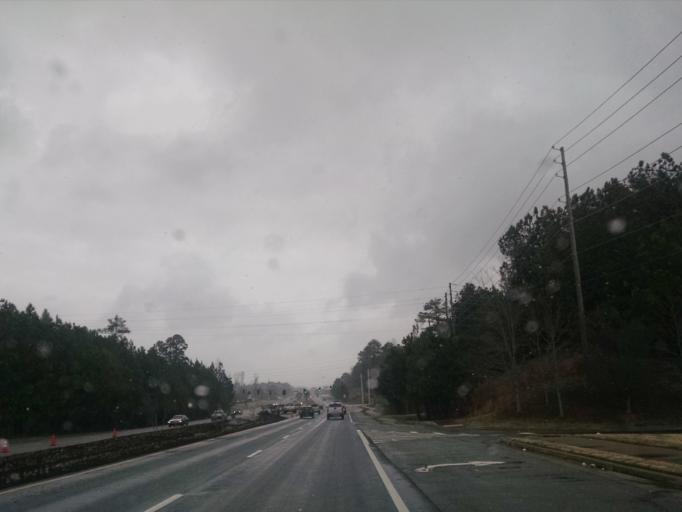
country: US
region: Georgia
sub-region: Gwinnett County
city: Suwanee
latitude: 34.0663
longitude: -84.0710
